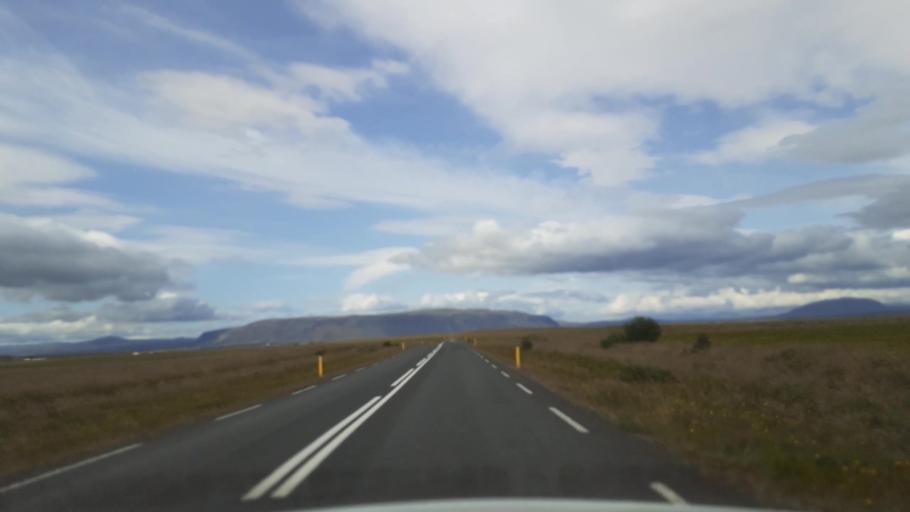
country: IS
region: South
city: Selfoss
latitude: 63.9065
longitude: -20.8194
